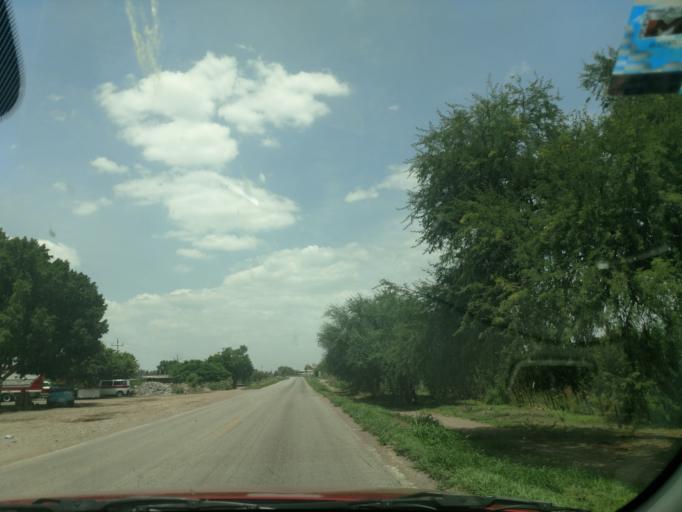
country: MX
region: San Luis Potosi
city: Ciudad Fernandez
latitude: 21.9526
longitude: -100.0666
